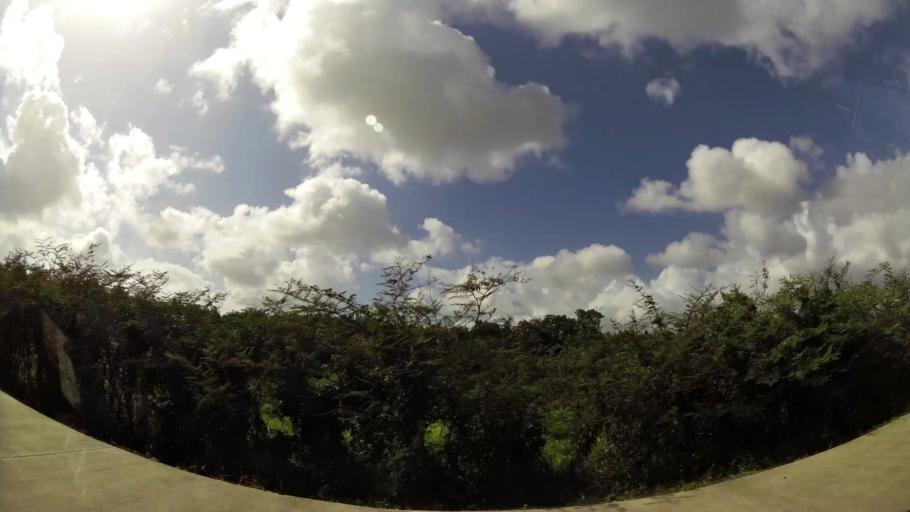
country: MQ
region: Martinique
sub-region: Martinique
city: Le Lamentin
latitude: 14.6172
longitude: -61.0054
